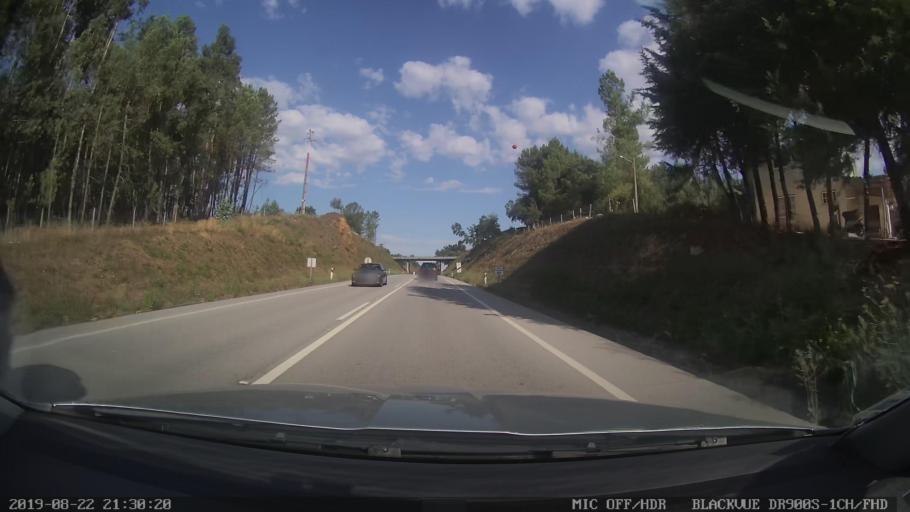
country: PT
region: Leiria
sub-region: Pedrogao Grande
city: Pedrogao Grande
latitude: 39.9090
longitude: -8.1493
